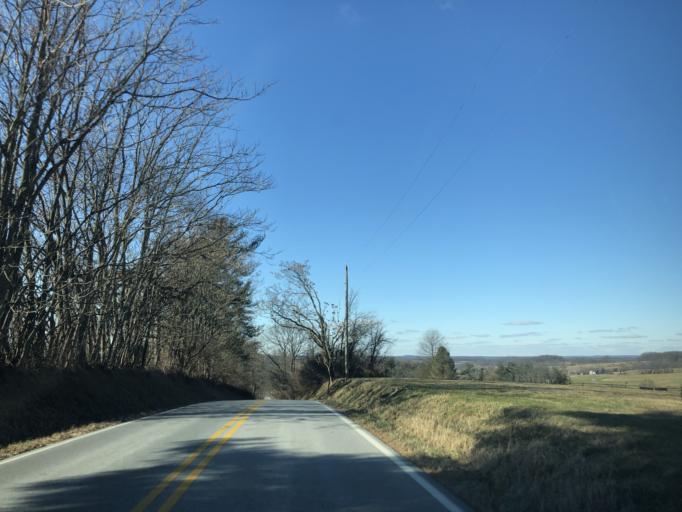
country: US
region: Pennsylvania
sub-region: Chester County
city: Upland
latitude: 39.9002
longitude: -75.7638
